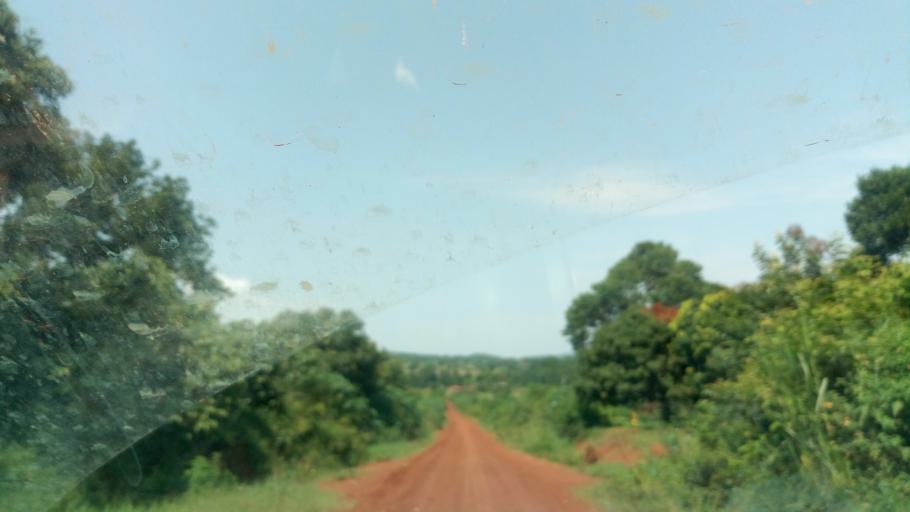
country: UG
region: Western Region
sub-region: Masindi District
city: Masindi
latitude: 1.6735
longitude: 31.8280
